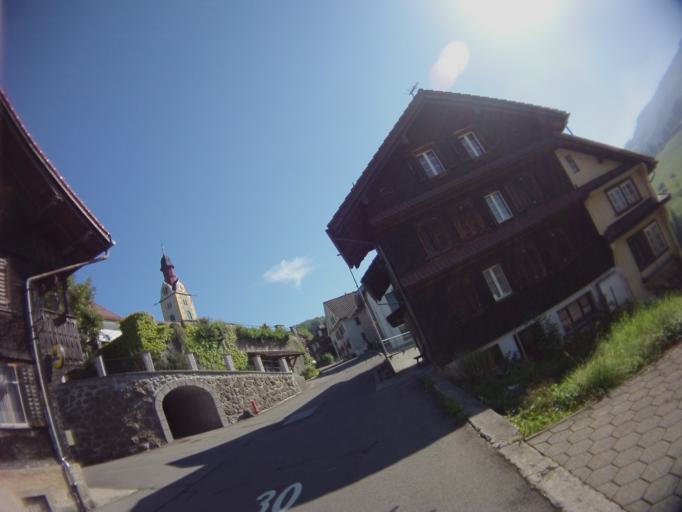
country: CH
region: Schwyz
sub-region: Bezirk Schwyz
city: Sattel
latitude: 47.0832
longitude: 8.6372
